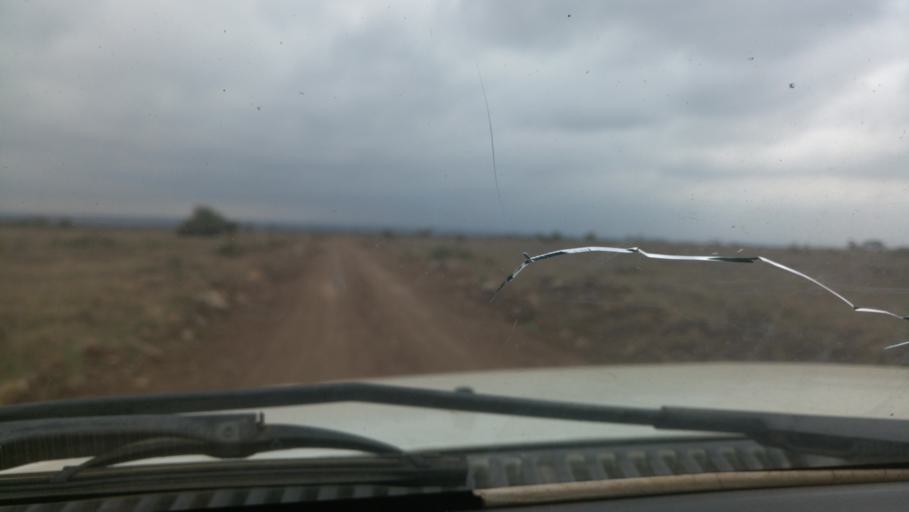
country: KE
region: Nairobi Area
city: Pumwani
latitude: -1.3892
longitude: 36.8496
